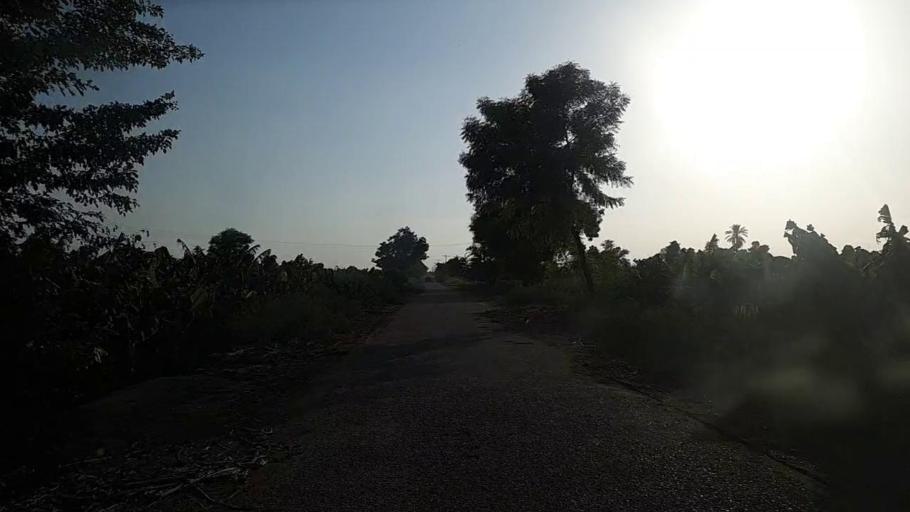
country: PK
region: Sindh
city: Hingorja
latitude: 27.0606
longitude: 68.4181
